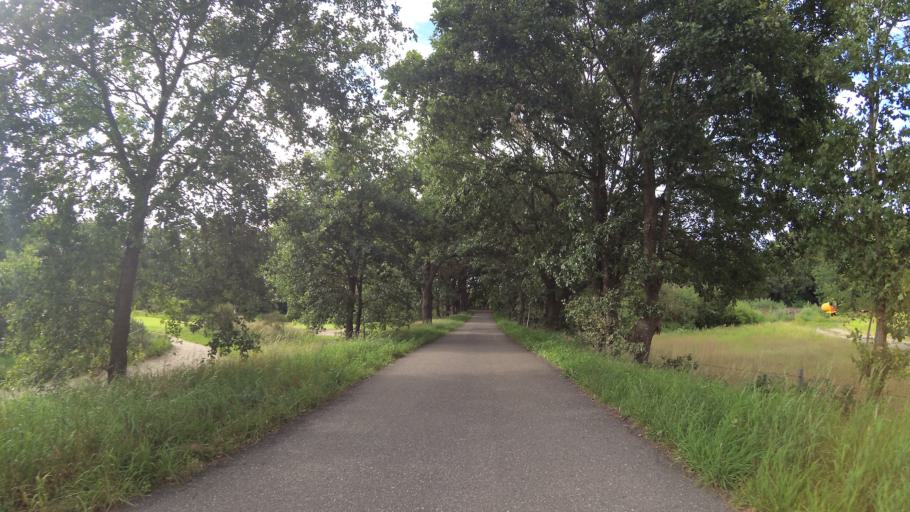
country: NL
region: North Brabant
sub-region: Gemeente Made en Drimmelen
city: Made
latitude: 51.6427
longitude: 4.8037
